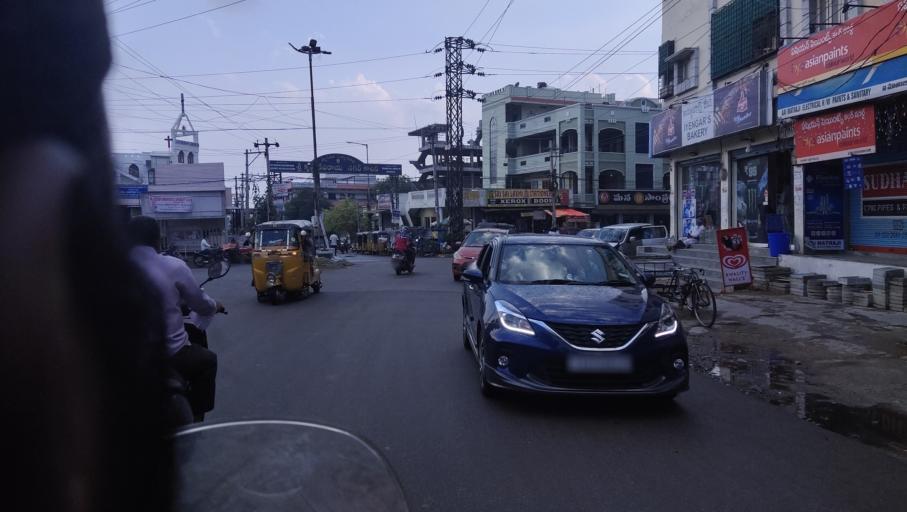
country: IN
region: Telangana
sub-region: Rangareddi
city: Lal Bahadur Nagar
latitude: 17.3216
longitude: 78.5650
